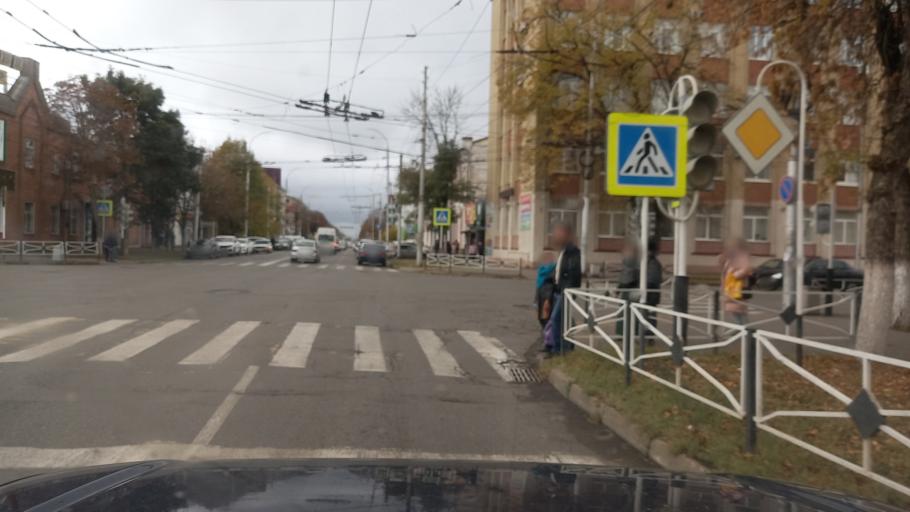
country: RU
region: Adygeya
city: Maykop
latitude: 44.6090
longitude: 40.1077
